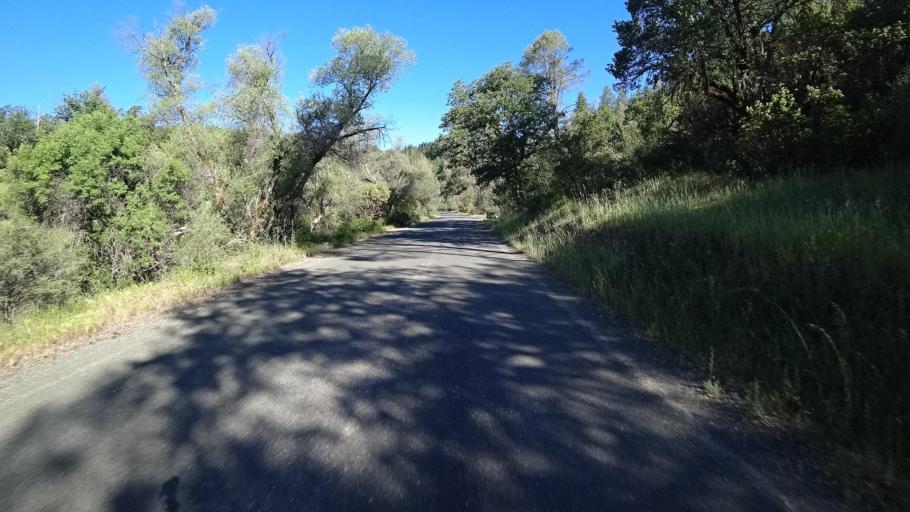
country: US
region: California
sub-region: Lake County
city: Upper Lake
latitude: 39.4160
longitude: -122.9760
